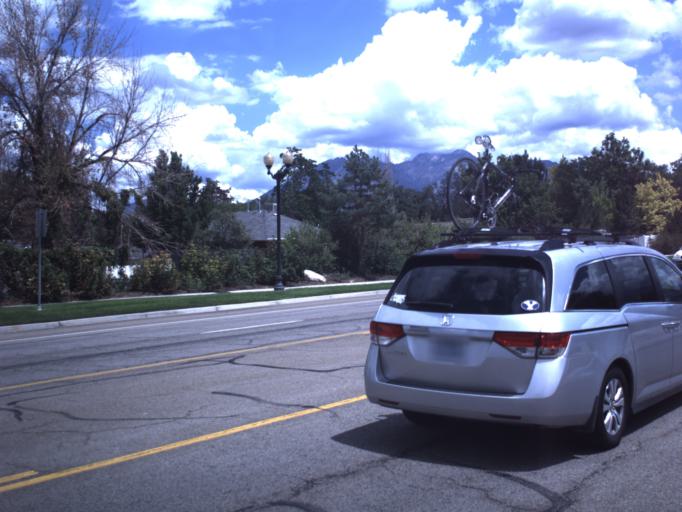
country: US
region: Utah
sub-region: Salt Lake County
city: Sandy City
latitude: 40.5881
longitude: -111.8835
